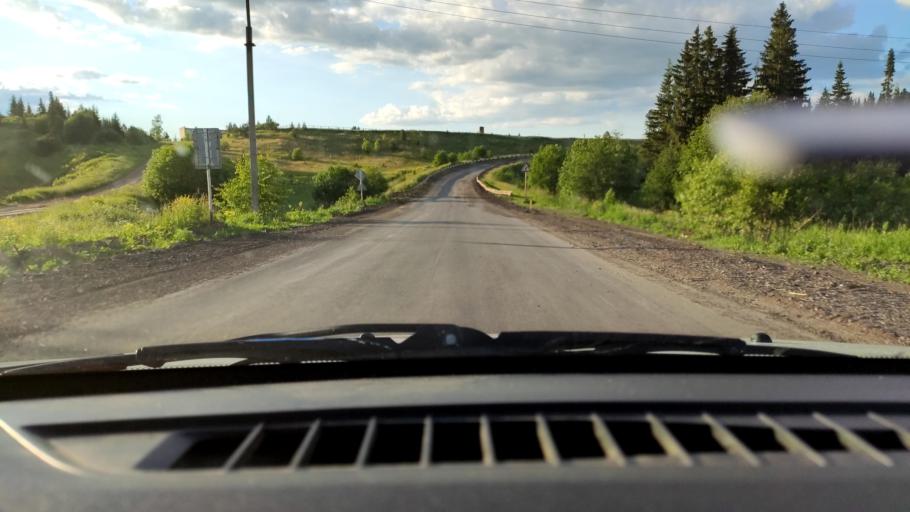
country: RU
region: Perm
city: Uinskoye
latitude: 57.1092
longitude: 56.5315
